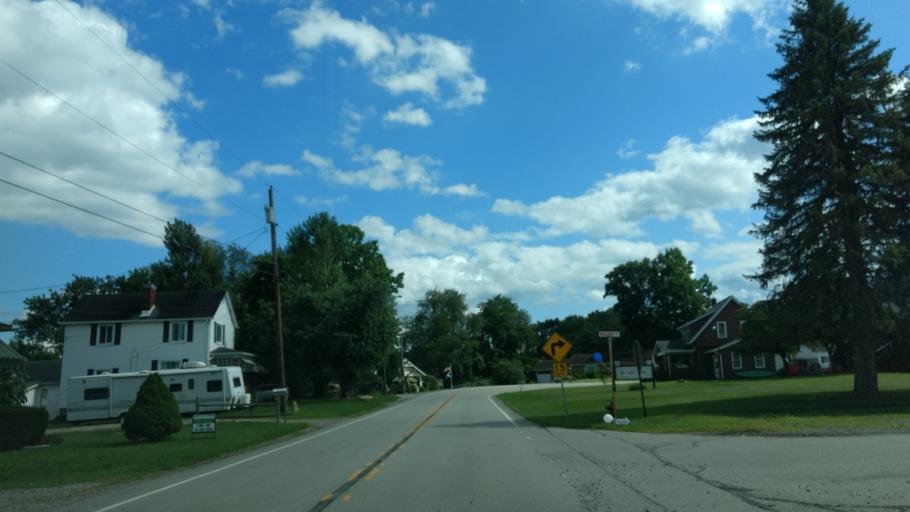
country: US
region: Pennsylvania
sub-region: Armstrong County
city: Apollo
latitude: 40.5766
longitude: -79.5707
